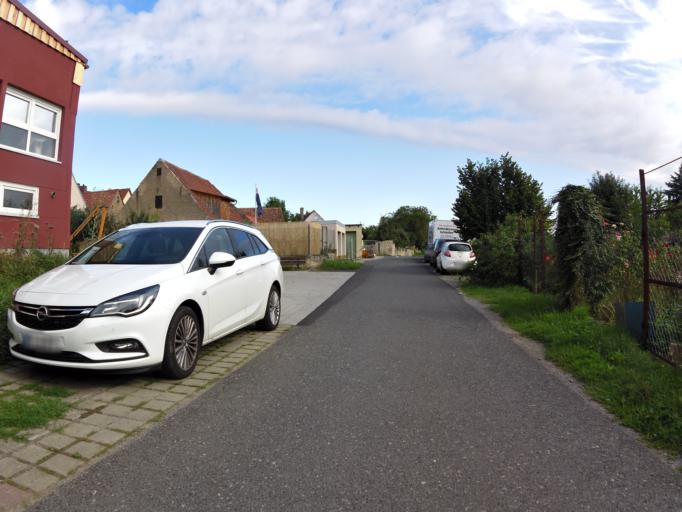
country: DE
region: Bavaria
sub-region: Regierungsbezirk Unterfranken
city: Mainstockheim
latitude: 49.7737
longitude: 10.1527
